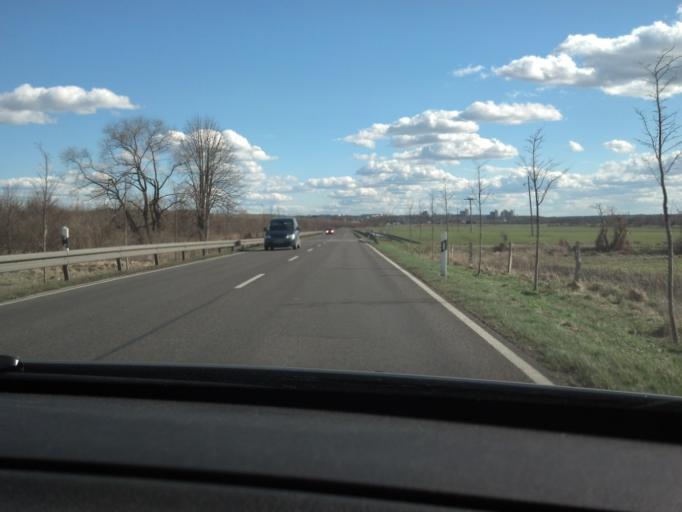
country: DE
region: Mecklenburg-Vorpommern
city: Trollenhagen
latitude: 53.6136
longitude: 13.2637
